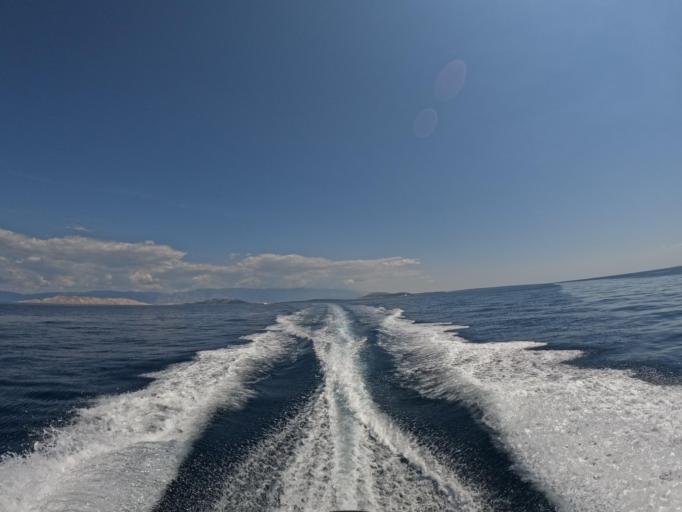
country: HR
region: Primorsko-Goranska
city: Punat
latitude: 44.8966
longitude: 14.6194
